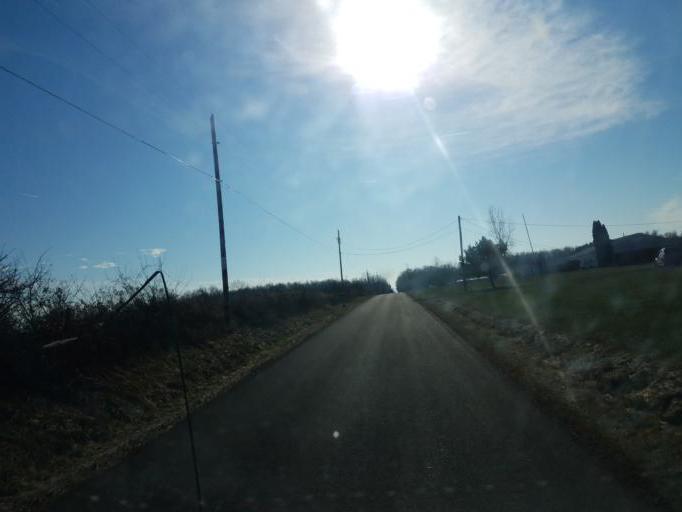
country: US
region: Ohio
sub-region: Morrow County
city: Cardington
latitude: 40.4938
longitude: -82.8679
